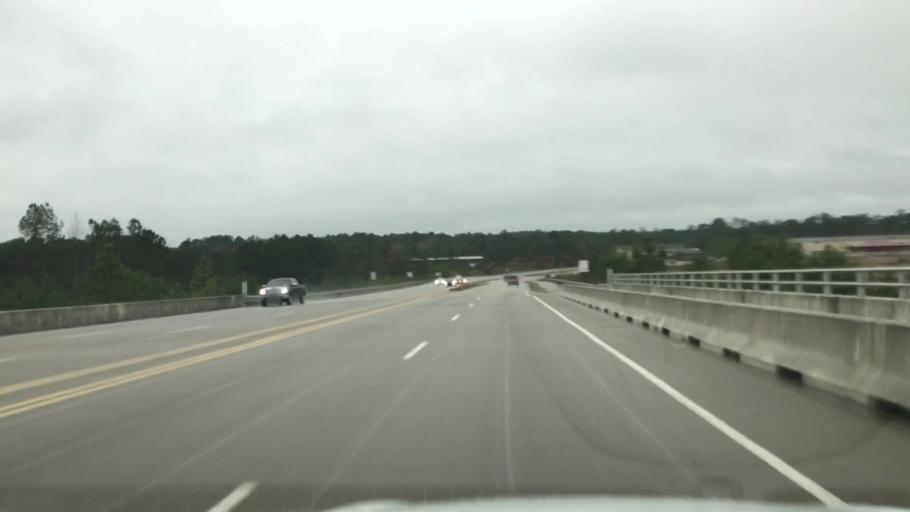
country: US
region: South Carolina
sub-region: Horry County
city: Forestbrook
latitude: 33.7068
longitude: -78.9369
